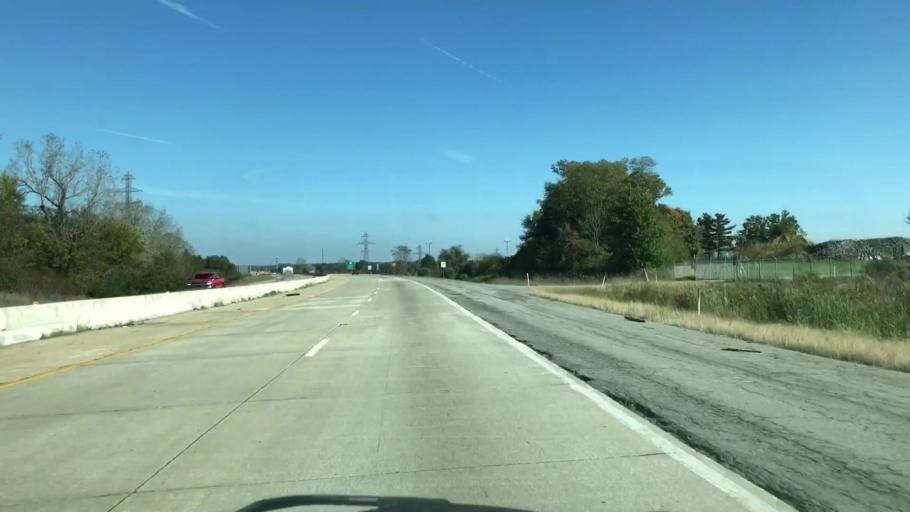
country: US
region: Indiana
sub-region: Elkhart County
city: Elkhart
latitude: 41.6395
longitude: -85.9697
